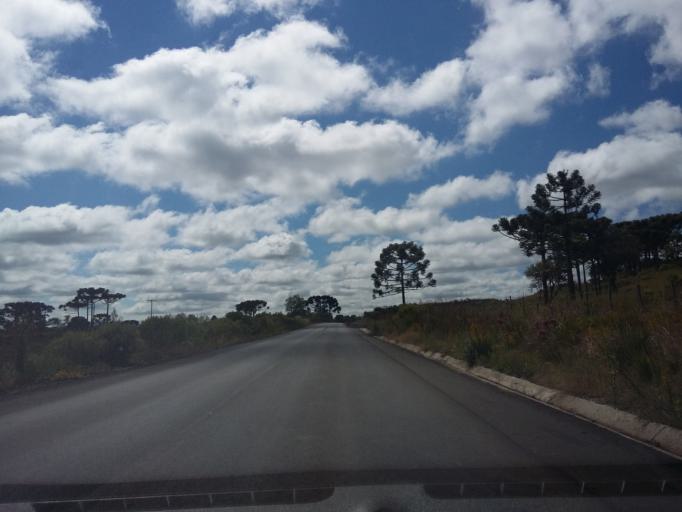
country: BR
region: Santa Catarina
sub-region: Sao Joaquim
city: Sao Joaquim
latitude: -28.2022
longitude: -49.9913
